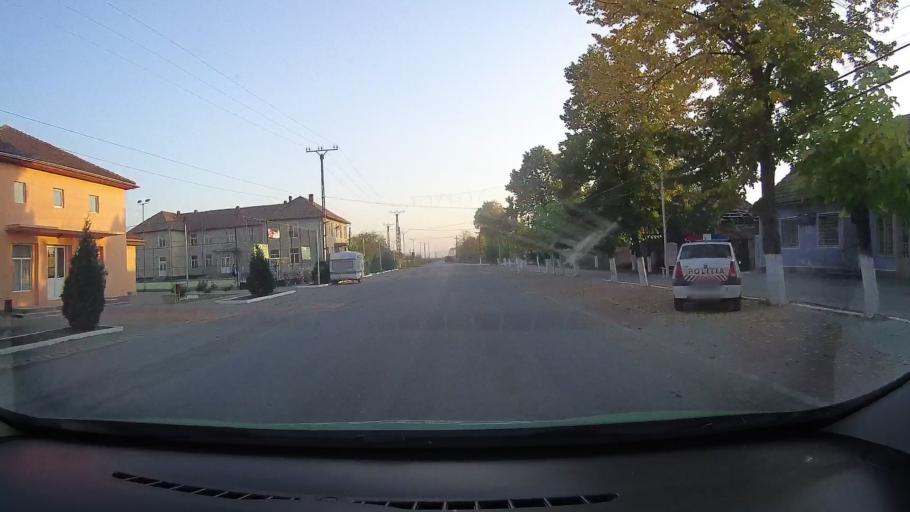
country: RO
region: Arad
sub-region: Comuna Sicula
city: Sicula
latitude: 46.4348
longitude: 21.7575
